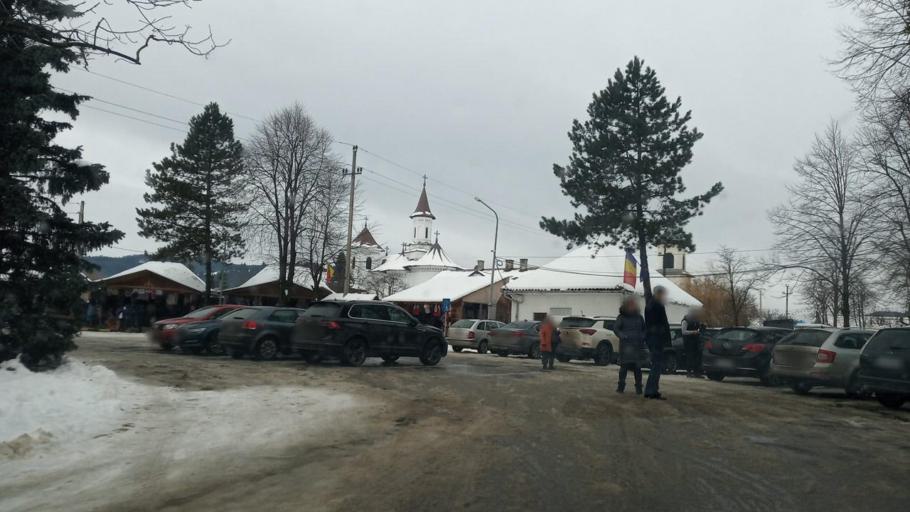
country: RO
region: Suceava
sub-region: Comuna Manastirea Humorului
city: Manastirea Humorului
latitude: 47.5943
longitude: 25.8568
